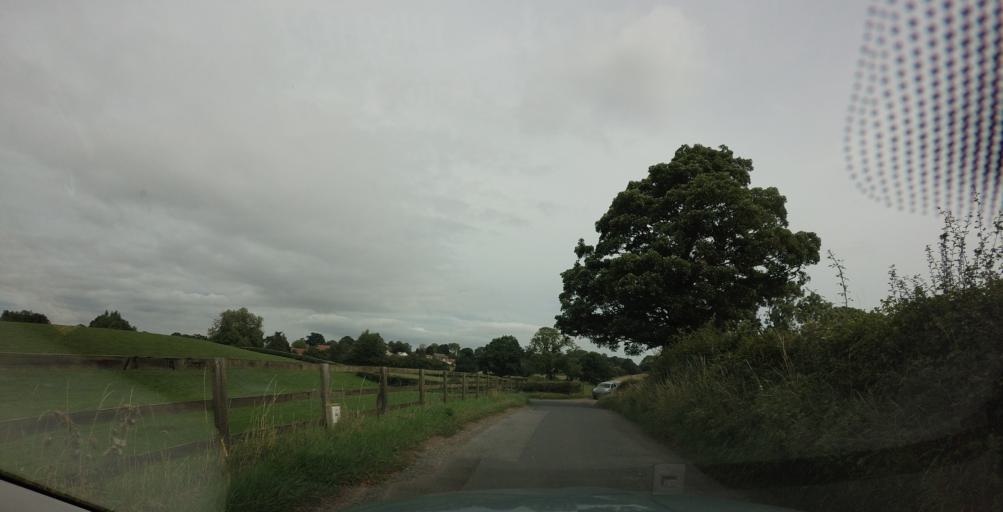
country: GB
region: England
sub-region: North Yorkshire
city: Ripon
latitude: 54.1329
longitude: -1.4823
